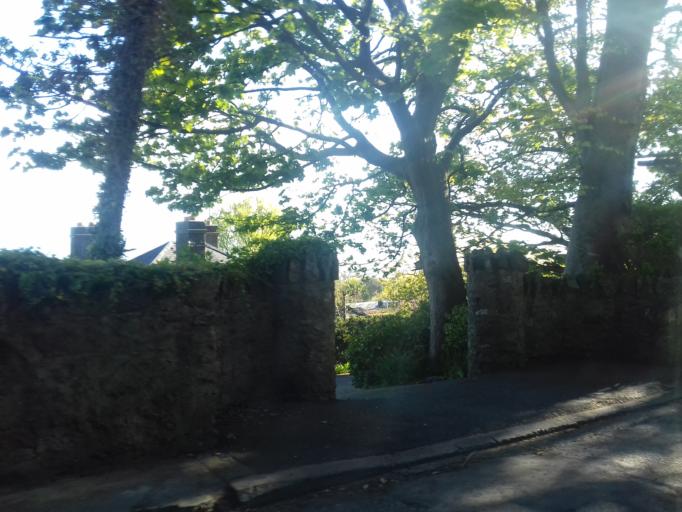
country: IE
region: Leinster
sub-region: Fingal County
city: Howth
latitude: 53.3667
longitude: -6.0751
